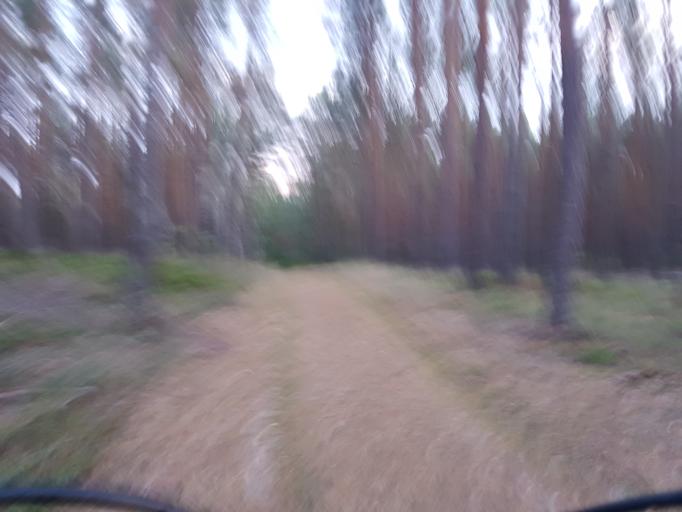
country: DE
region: Brandenburg
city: Trobitz
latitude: 51.5674
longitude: 13.4523
